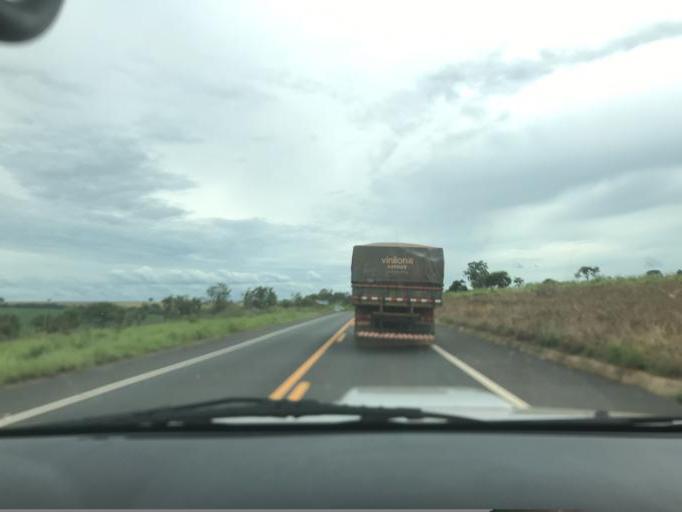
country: BR
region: Minas Gerais
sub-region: Araxa
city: Araxa
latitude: -19.3694
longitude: -46.8555
